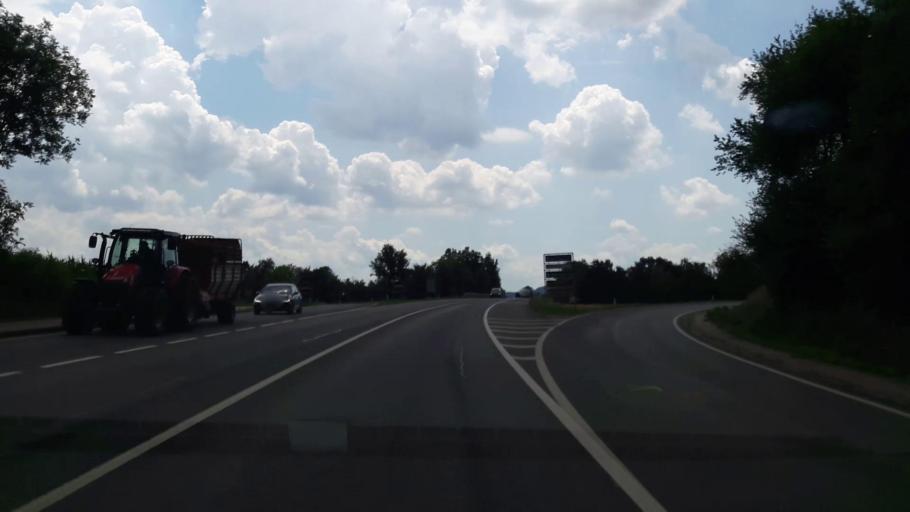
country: AT
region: Lower Austria
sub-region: Politischer Bezirk Melk
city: Emmersdorf an der Donau
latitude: 48.2363
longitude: 15.3490
